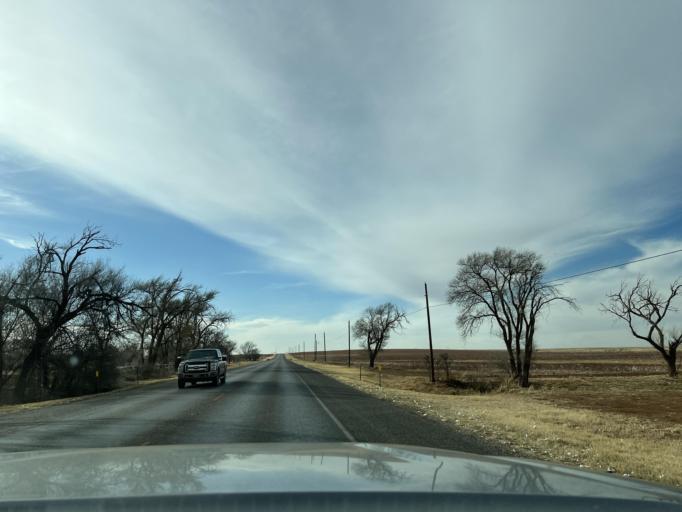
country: US
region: Texas
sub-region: Fisher County
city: Roby
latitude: 32.7409
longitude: -100.4802
